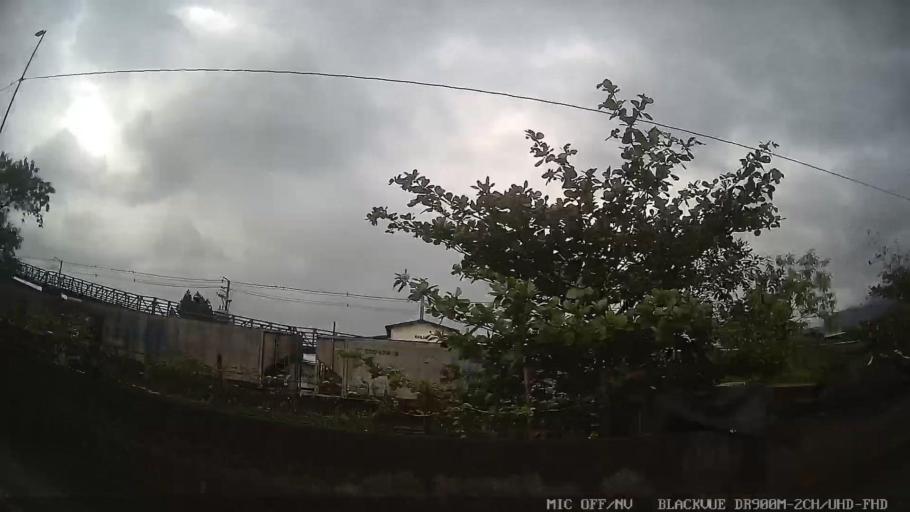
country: BR
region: Sao Paulo
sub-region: Cubatao
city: Cubatao
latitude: -23.8988
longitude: -46.4470
